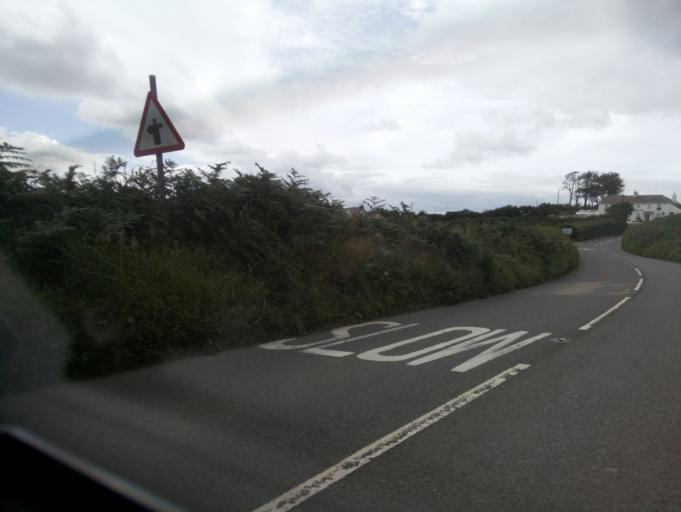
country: GB
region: England
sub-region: Devon
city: Dartmouth
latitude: 50.3578
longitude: -3.6428
